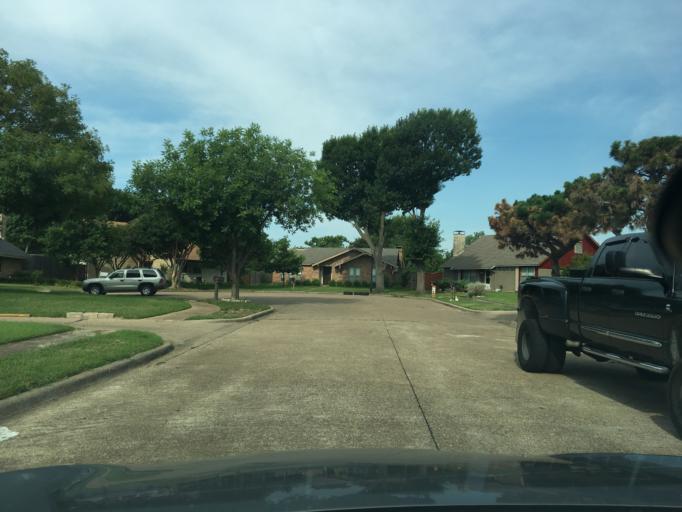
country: US
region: Texas
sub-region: Dallas County
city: Richardson
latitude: 32.9648
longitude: -96.6739
